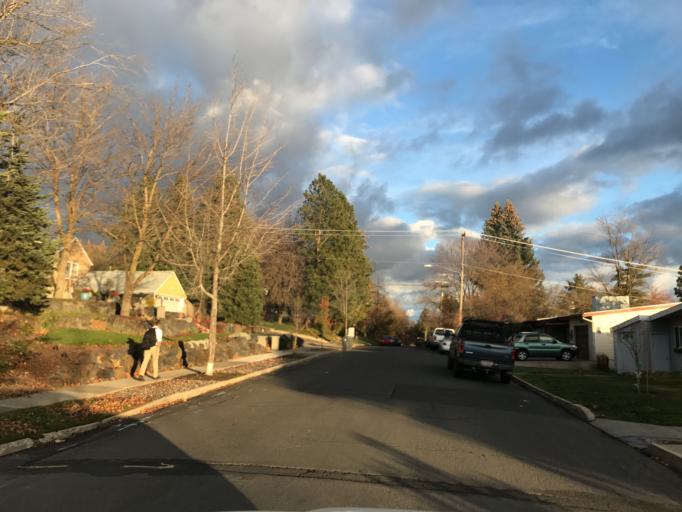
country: US
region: Idaho
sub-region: Latah County
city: Moscow
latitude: 46.7360
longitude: -117.0129
